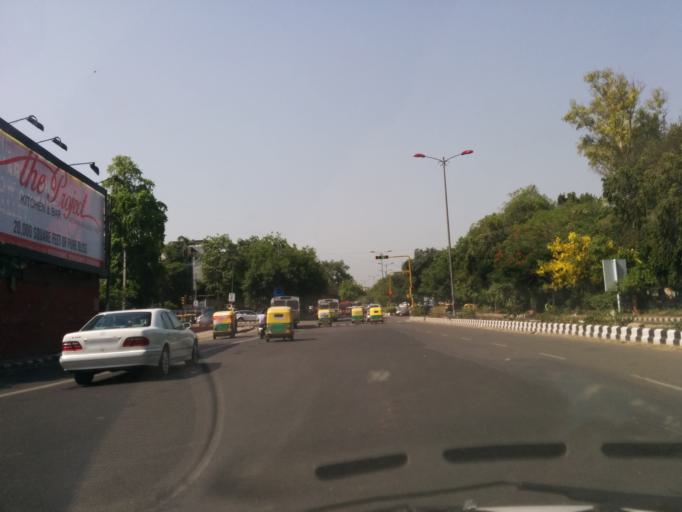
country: IN
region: NCT
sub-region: New Delhi
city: New Delhi
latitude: 28.5544
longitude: 77.2057
